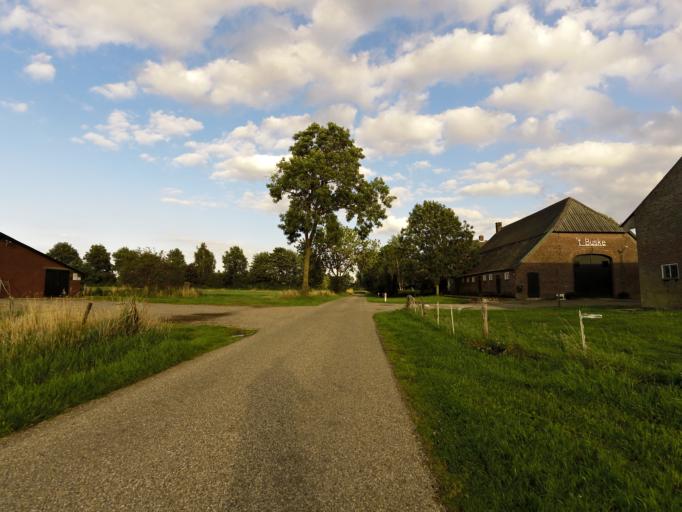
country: NL
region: Gelderland
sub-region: Gemeente Doesburg
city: Doesburg
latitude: 51.9763
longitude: 6.1909
